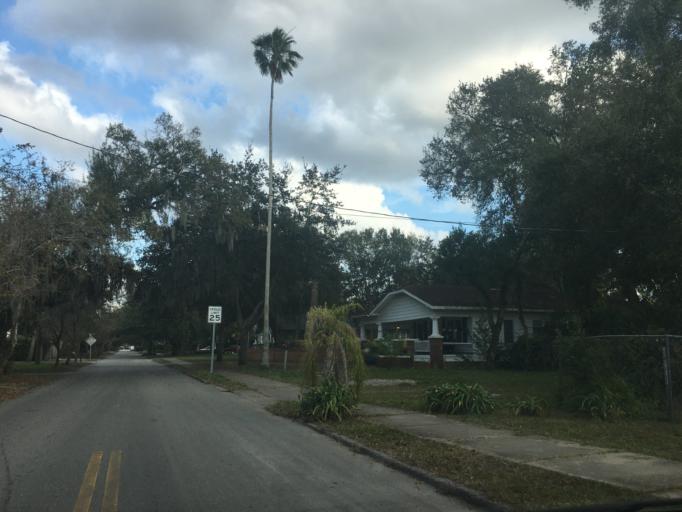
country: US
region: Florida
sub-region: Hillsborough County
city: Egypt Lake-Leto
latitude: 27.9997
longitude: -82.4634
